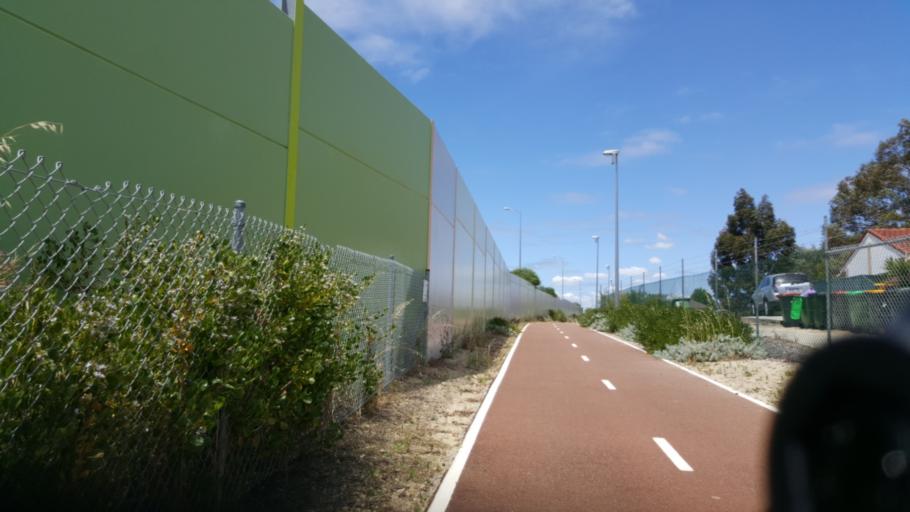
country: AU
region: Western Australia
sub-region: Bayswater
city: Embleton
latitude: -31.8684
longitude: 115.8927
